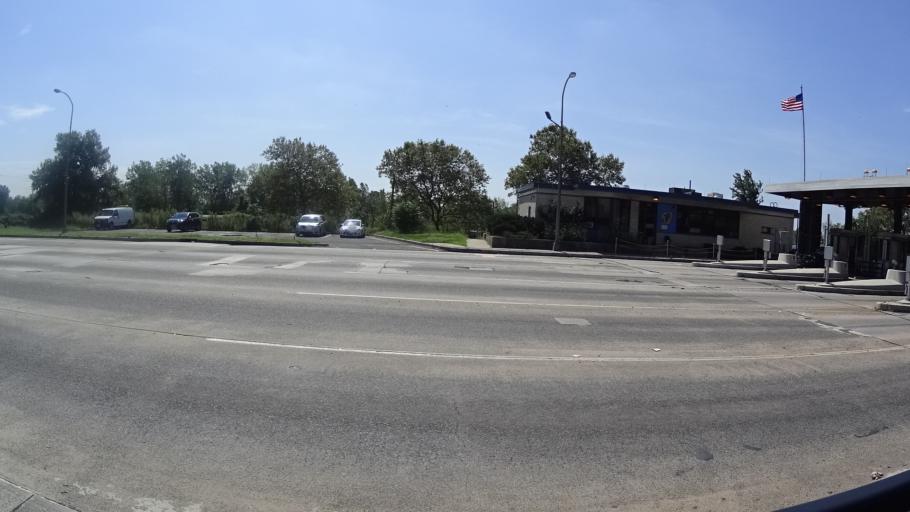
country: US
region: New Jersey
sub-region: Hudson County
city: Jersey City
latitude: 40.7064
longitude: -74.0617
